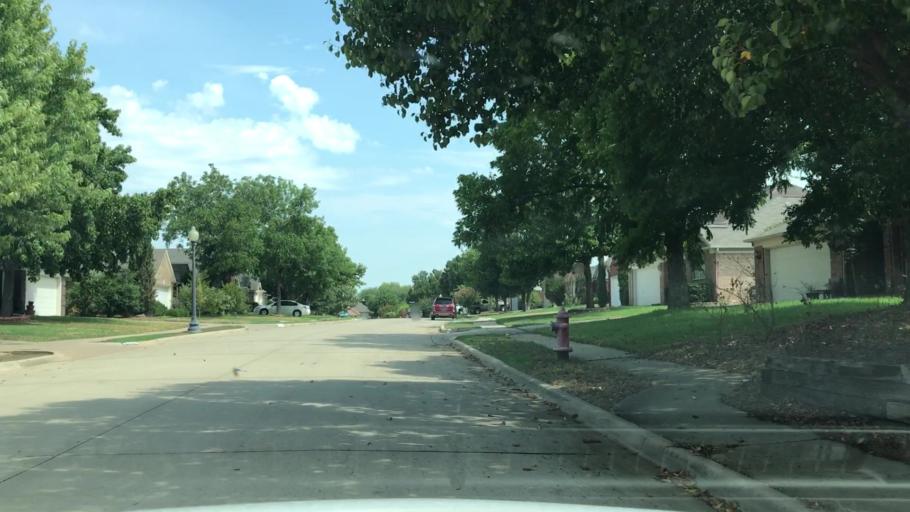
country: US
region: Texas
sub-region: Tarrant County
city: Euless
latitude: 32.8529
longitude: -97.0798
